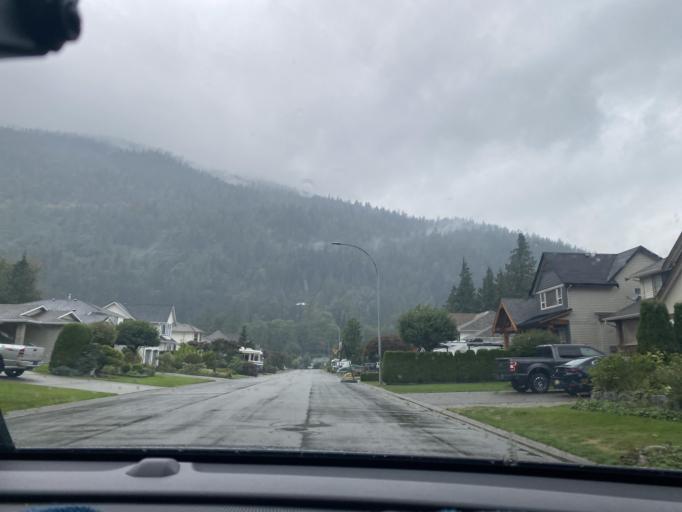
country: CA
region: British Columbia
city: Agassiz
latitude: 49.2955
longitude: -121.7789
